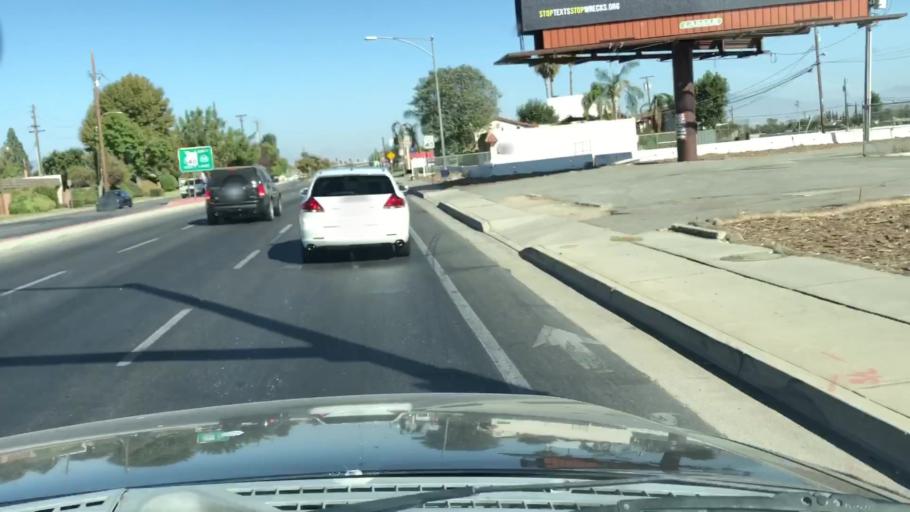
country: US
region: California
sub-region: Kern County
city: Bakersfield
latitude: 35.3541
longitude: -119.0476
